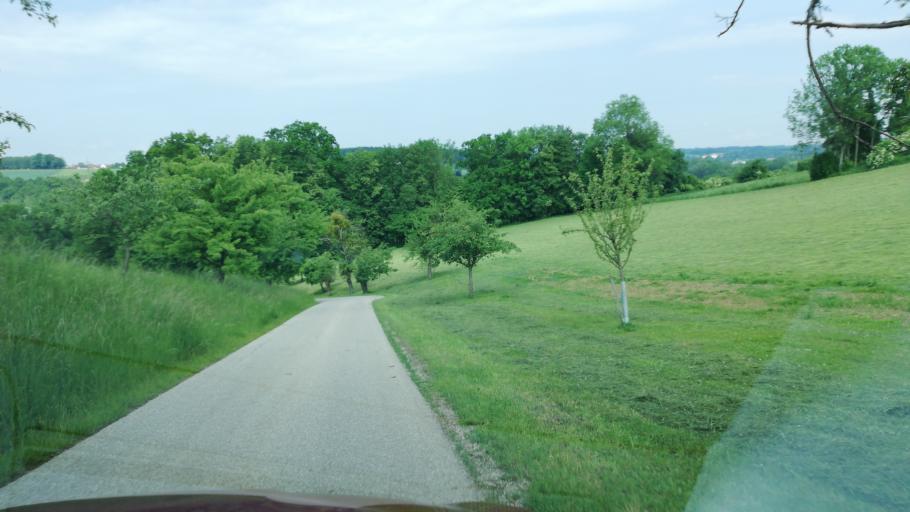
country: AT
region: Upper Austria
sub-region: Politischer Bezirk Steyr-Land
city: Bad Hall
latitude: 48.0492
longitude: 14.2130
